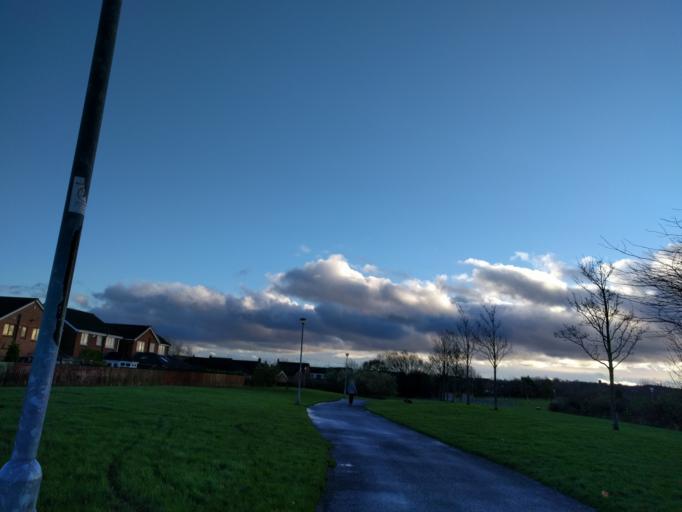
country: GB
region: England
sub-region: Northumberland
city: Cramlington
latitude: 55.1010
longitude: -1.5807
